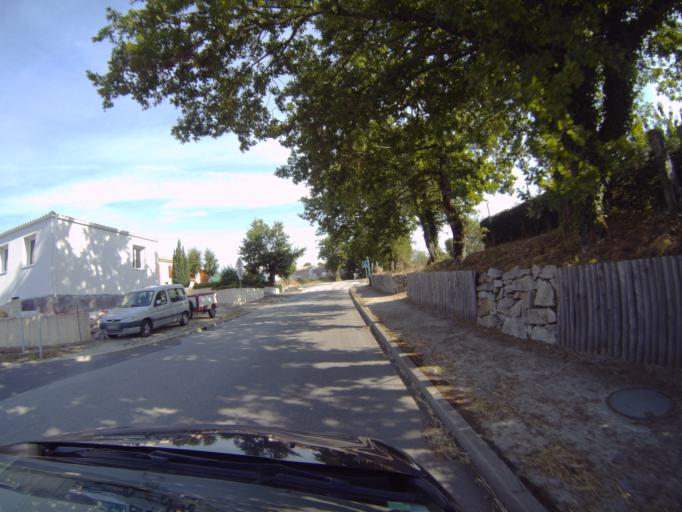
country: FR
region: Pays de la Loire
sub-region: Departement de la Vendee
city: Les Clouzeaux
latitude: 46.6347
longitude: -1.5100
